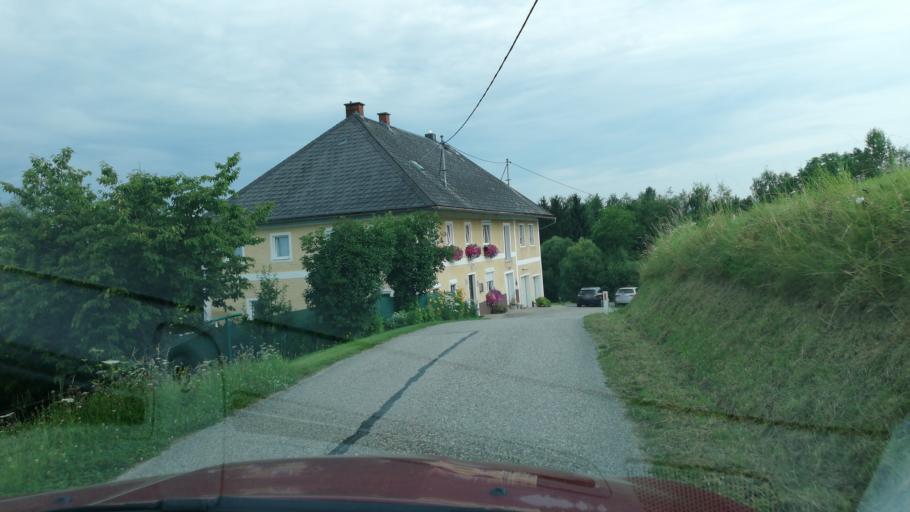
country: AT
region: Upper Austria
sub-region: Politischer Bezirk Rohrbach
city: Kleinzell im Muehlkreis
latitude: 48.5027
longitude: 14.0145
